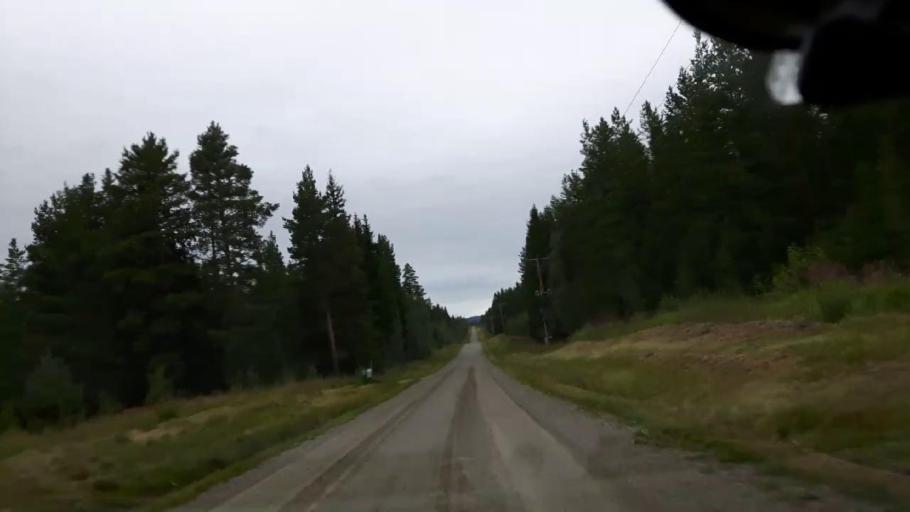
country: SE
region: Vaesternorrland
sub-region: Ange Kommun
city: Fransta
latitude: 62.7983
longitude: 16.0262
